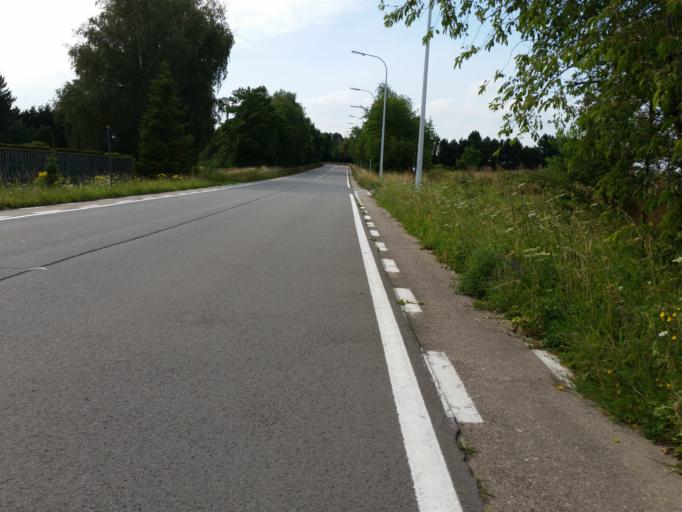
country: BE
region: Flanders
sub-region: Provincie Antwerpen
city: Rumst
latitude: 51.0941
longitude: 4.4443
